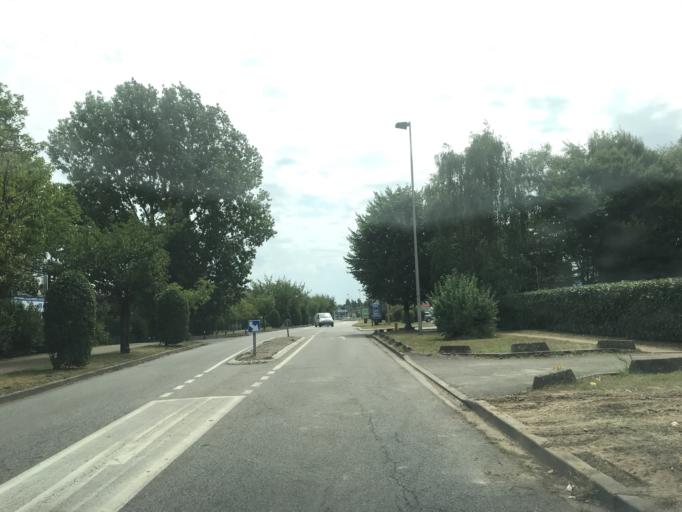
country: FR
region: Ile-de-France
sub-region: Departement des Yvelines
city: Maurepas
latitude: 48.7586
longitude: 1.9367
